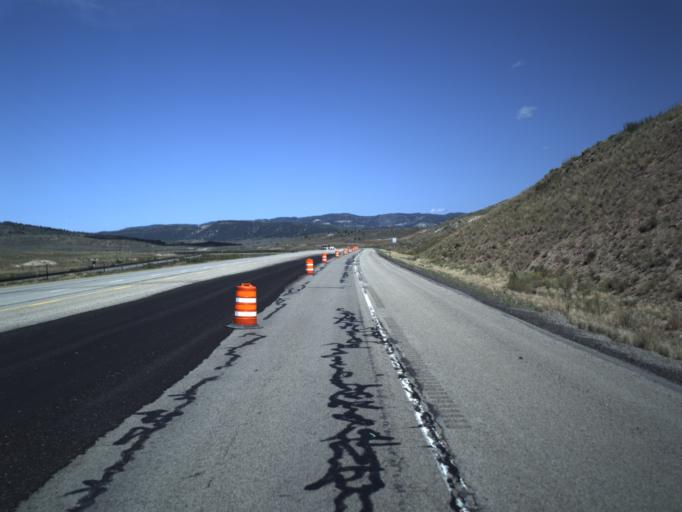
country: US
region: Utah
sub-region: Carbon County
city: Helper
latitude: 39.8674
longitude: -111.0306
